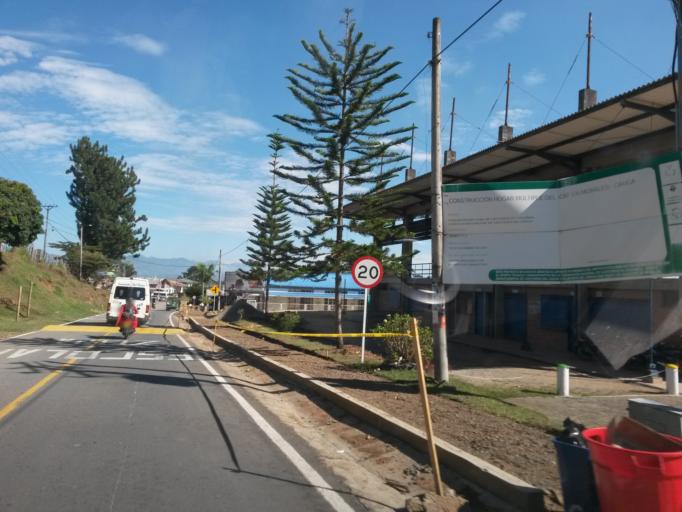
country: CO
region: Cauca
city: Morales
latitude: 2.7504
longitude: -76.6267
